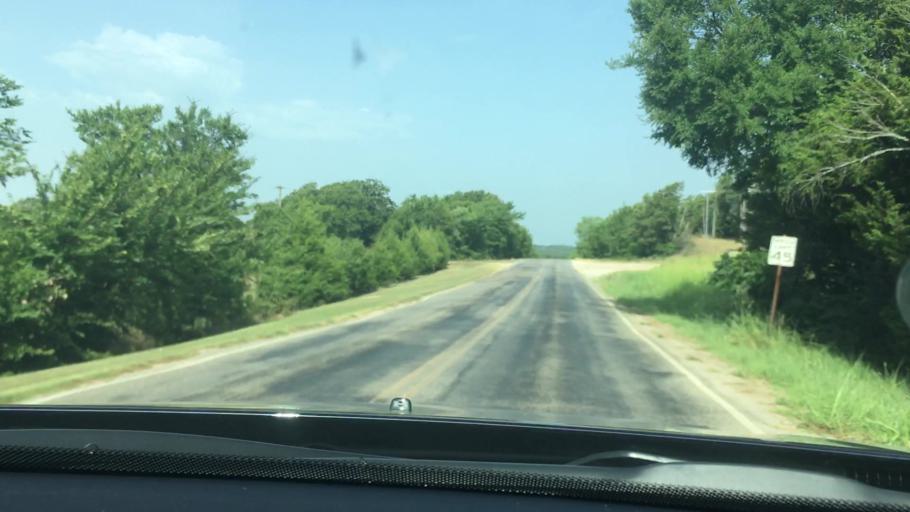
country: US
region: Oklahoma
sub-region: Pontotoc County
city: Byng
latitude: 34.8648
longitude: -96.6143
